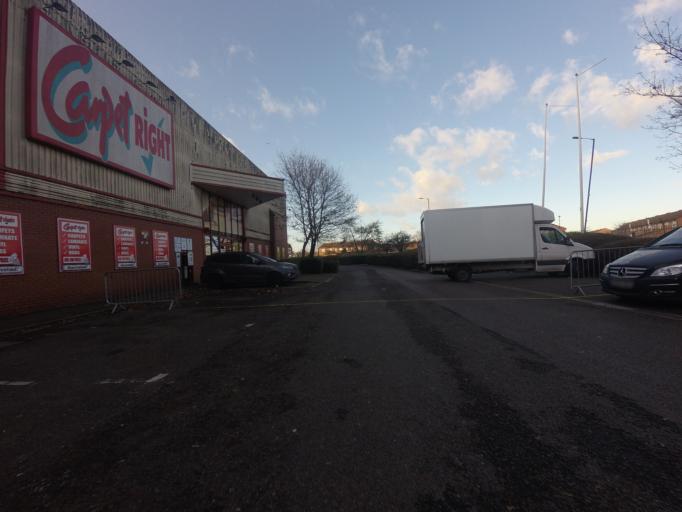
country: GB
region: England
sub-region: Greater London
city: Poplar
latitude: 51.5168
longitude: 0.0071
